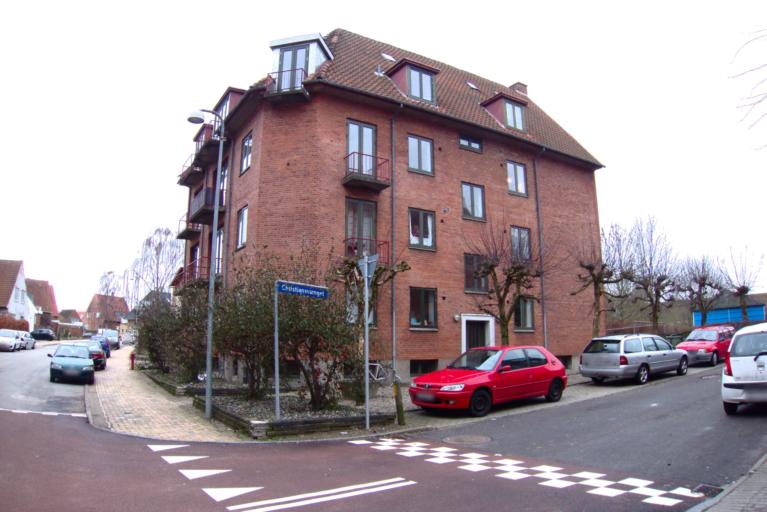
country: DK
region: South Denmark
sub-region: Odense Kommune
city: Odense
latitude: 55.3961
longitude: 10.4072
